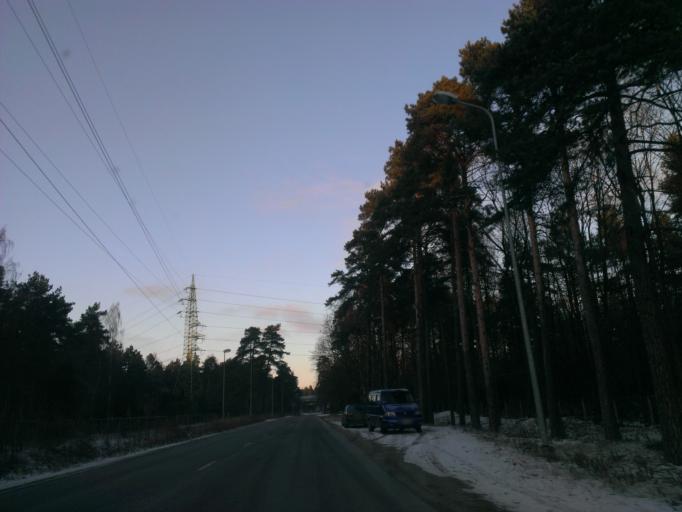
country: LV
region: Riga
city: Jaunciems
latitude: 56.9923
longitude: 24.1406
